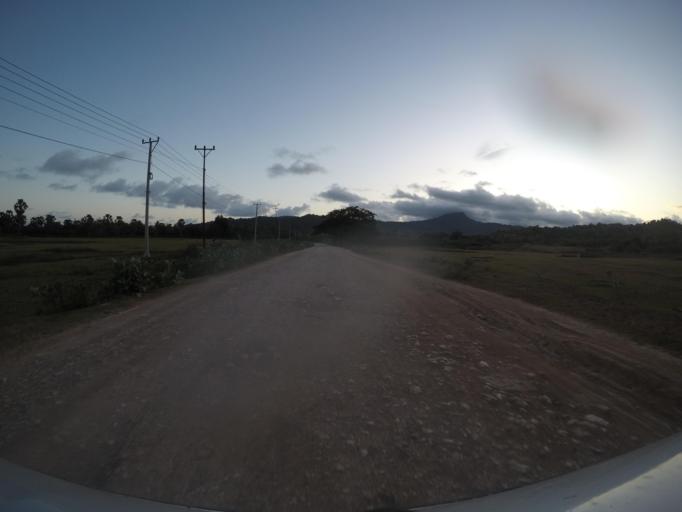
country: TL
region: Viqueque
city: Viqueque
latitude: -8.7707
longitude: 126.6420
